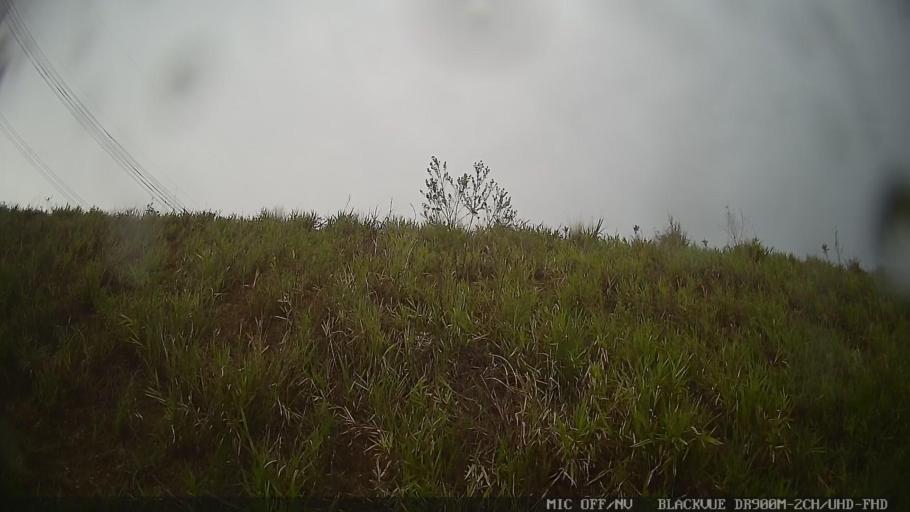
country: BR
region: Sao Paulo
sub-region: Pedreira
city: Pedreira
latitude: -22.7320
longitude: -46.8625
